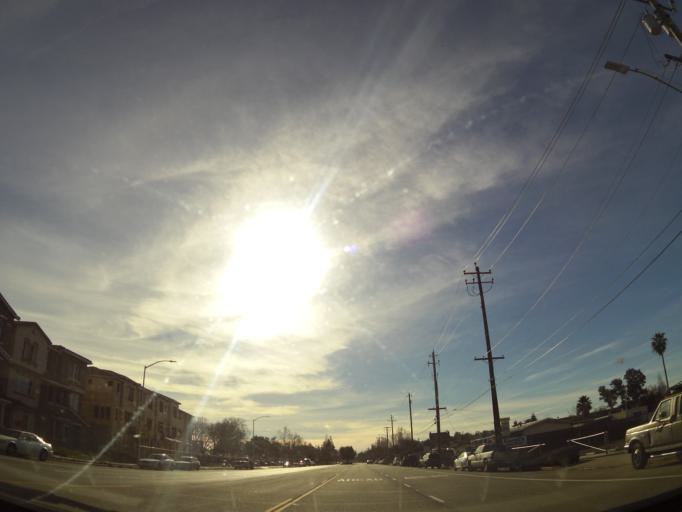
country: US
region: California
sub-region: Santa Clara County
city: Morgan Hill
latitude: 37.1372
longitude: -121.6603
